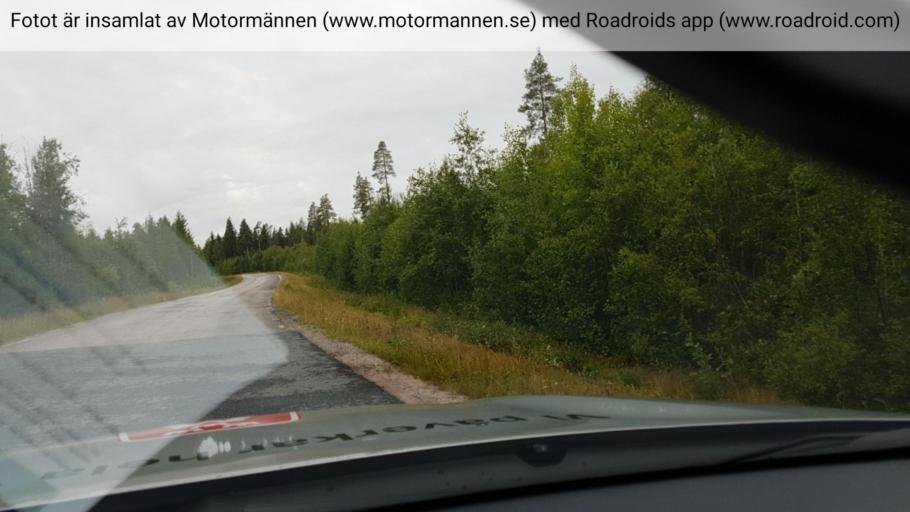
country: SE
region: Norrbotten
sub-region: Bodens Kommun
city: Saevast
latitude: 65.6670
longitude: 21.7575
